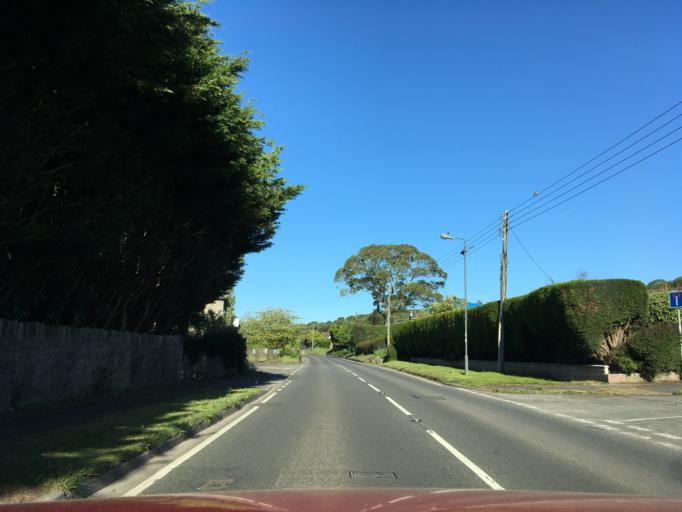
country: GB
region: England
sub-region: North Somerset
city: Nailsea
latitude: 51.4432
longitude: -2.8055
